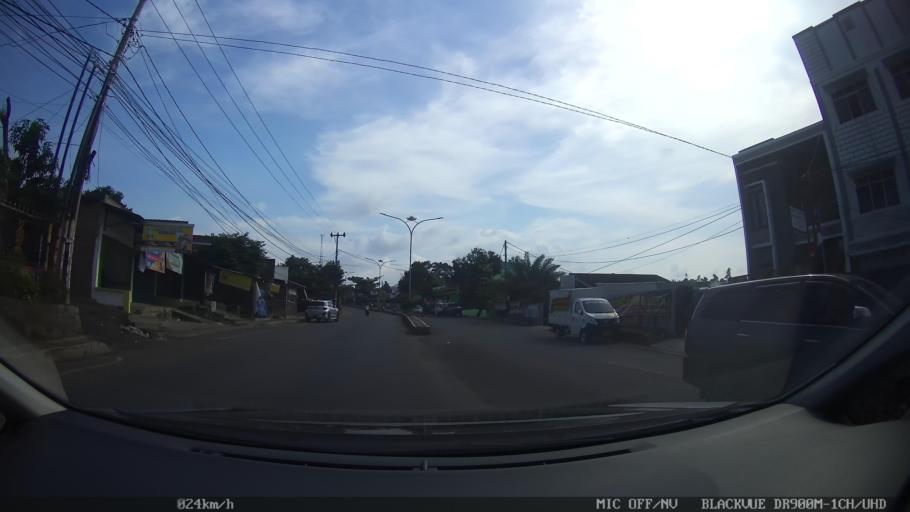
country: ID
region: Lampung
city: Kedaton
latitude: -5.3865
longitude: 105.2211
